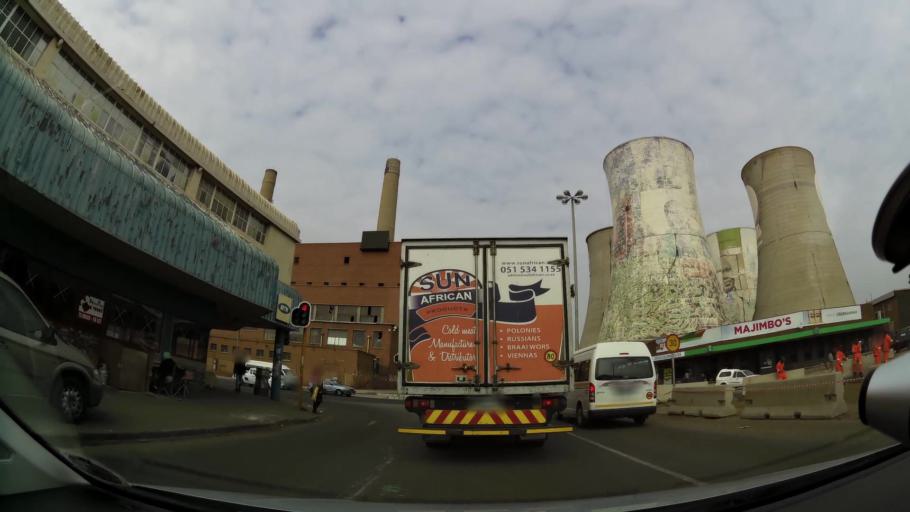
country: ZA
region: Orange Free State
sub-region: Mangaung Metropolitan Municipality
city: Bloemfontein
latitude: -29.1230
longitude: 26.2247
